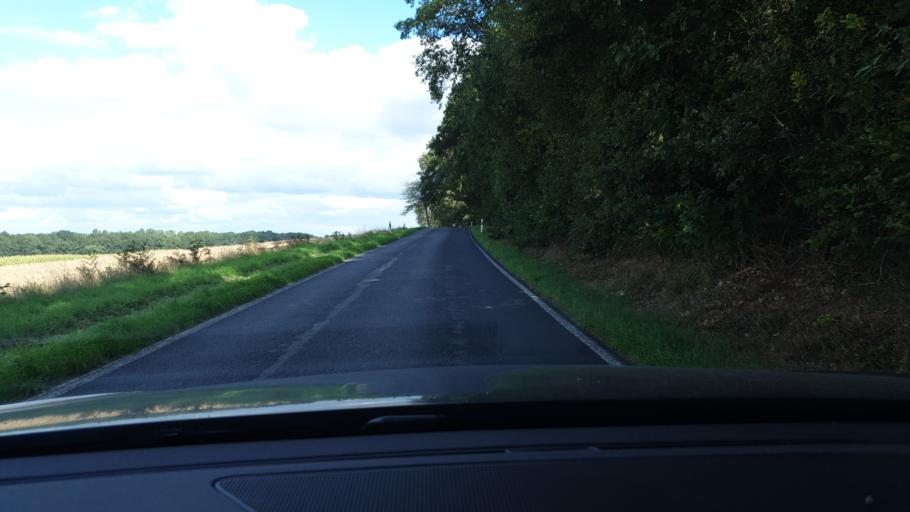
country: NL
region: Gelderland
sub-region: Gemeente Groesbeek
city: De Horst
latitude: 51.7684
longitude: 5.9913
